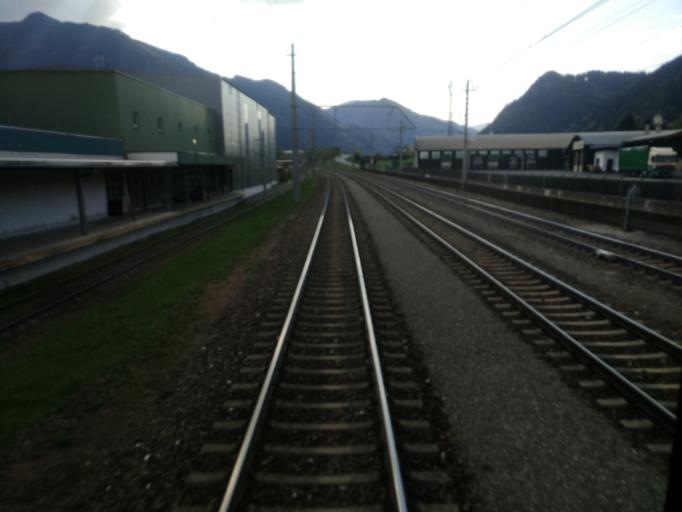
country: AT
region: Styria
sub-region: Politischer Bezirk Leoben
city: Mautern in Steiermark
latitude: 47.3968
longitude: 14.8340
